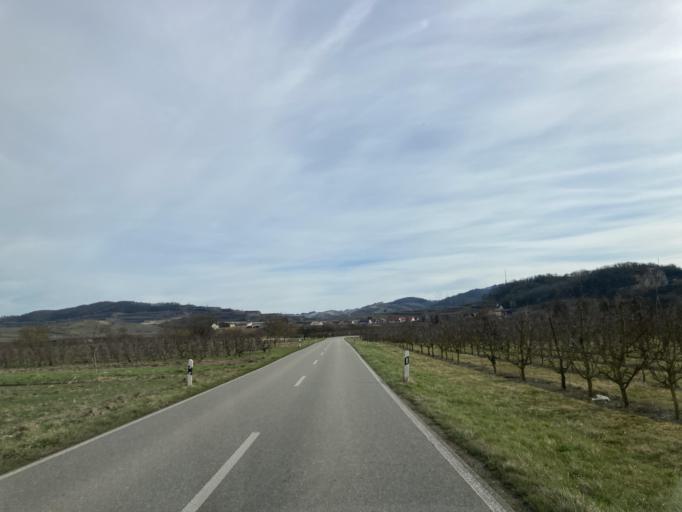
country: DE
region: Baden-Wuerttemberg
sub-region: Freiburg Region
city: Vogtsburg
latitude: 48.0854
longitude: 7.6022
